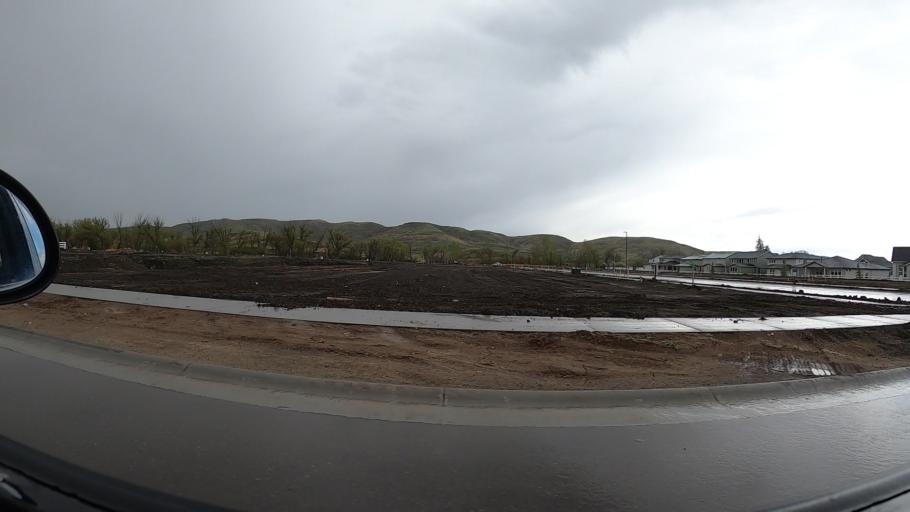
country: US
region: Idaho
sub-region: Ada County
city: Eagle
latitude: 43.7331
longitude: -116.2859
